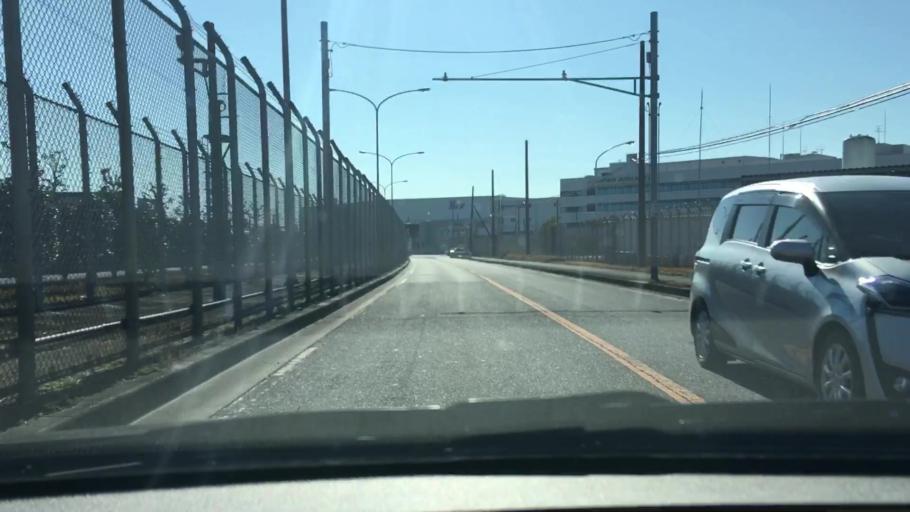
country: JP
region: Chiba
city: Narita
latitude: 35.7515
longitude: 140.4006
